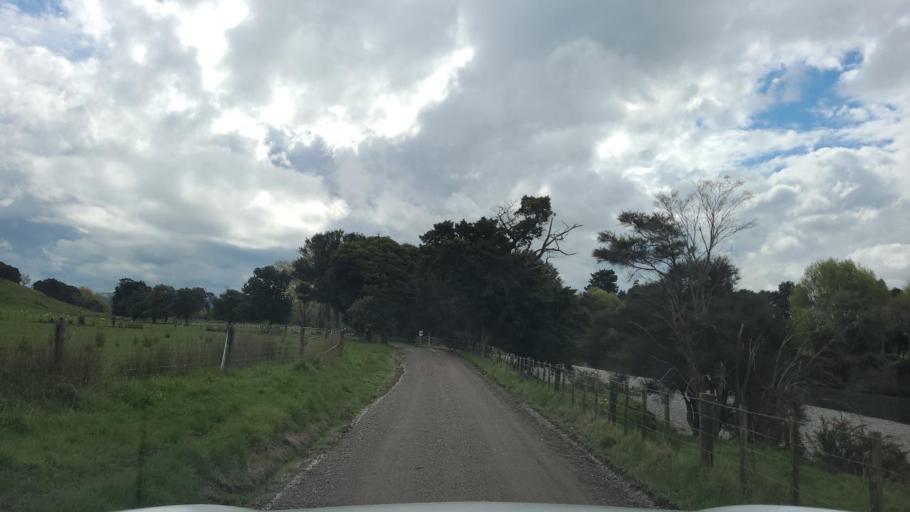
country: NZ
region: Wellington
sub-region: Masterton District
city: Masterton
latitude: -41.1000
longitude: 175.5365
